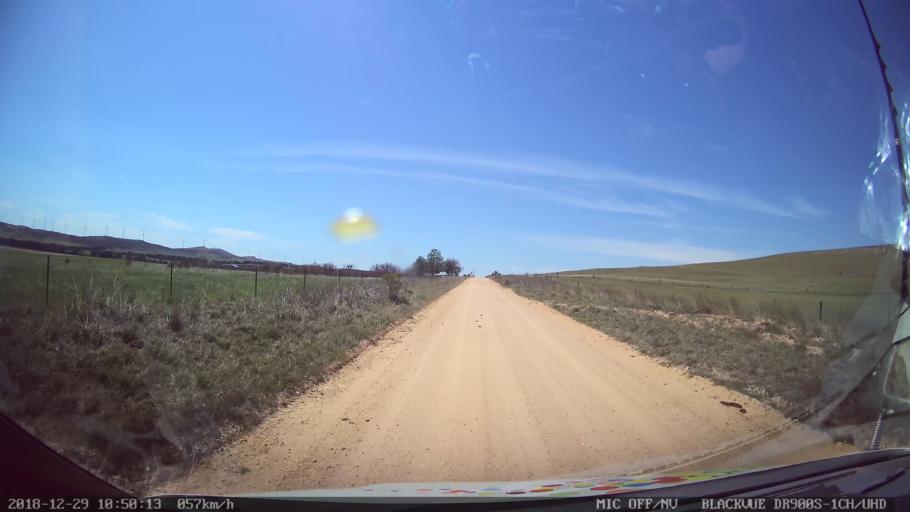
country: AU
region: New South Wales
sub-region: Palerang
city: Bungendore
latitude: -35.0805
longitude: 149.5210
